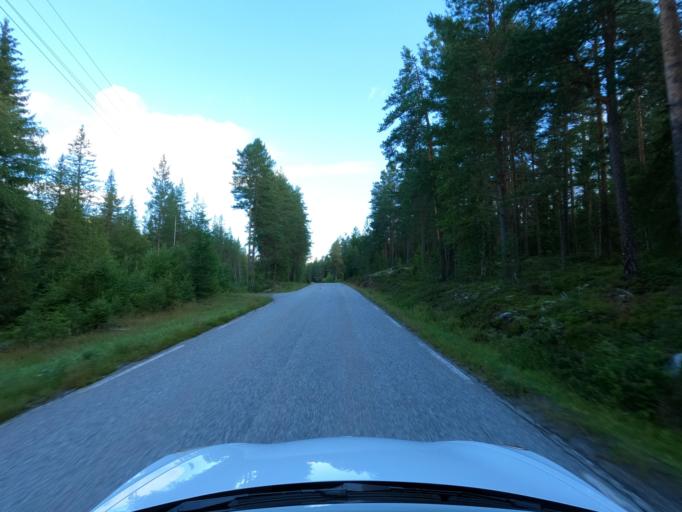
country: NO
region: Telemark
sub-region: Hjartdal
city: Sauland
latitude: 59.8216
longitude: 9.0660
